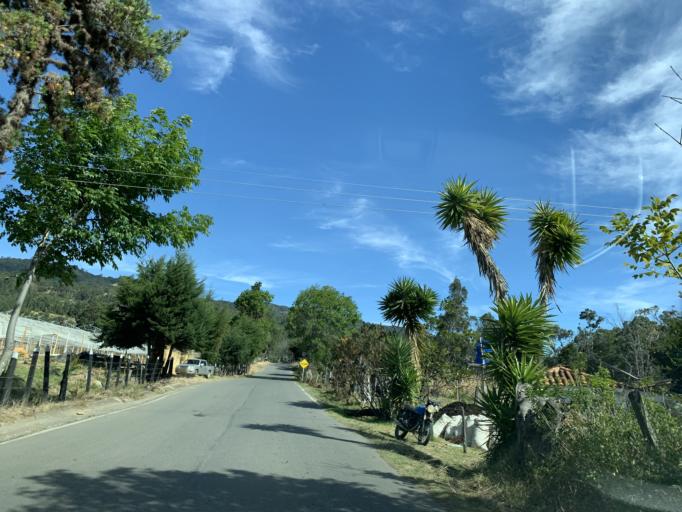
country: CO
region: Boyaca
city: Santa Sofia
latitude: 5.7073
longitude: -73.6004
